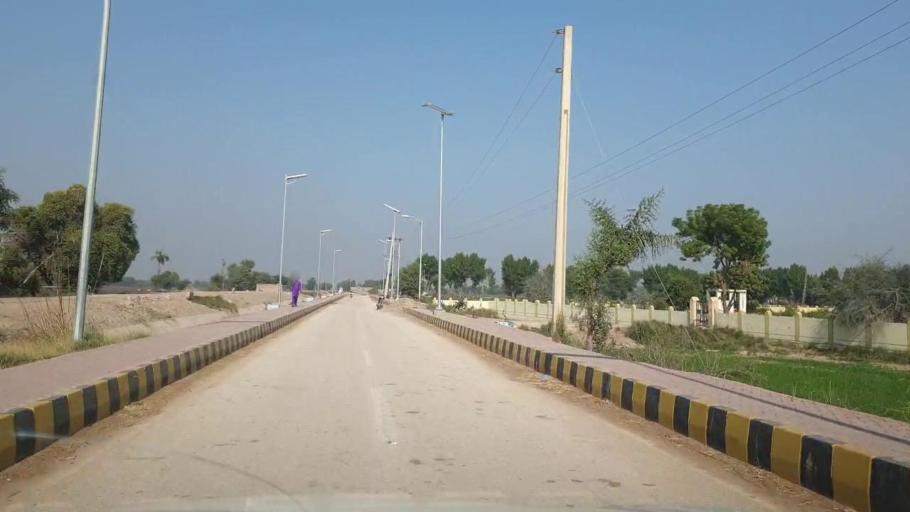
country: PK
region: Sindh
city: Bhan
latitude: 26.5377
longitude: 67.7757
